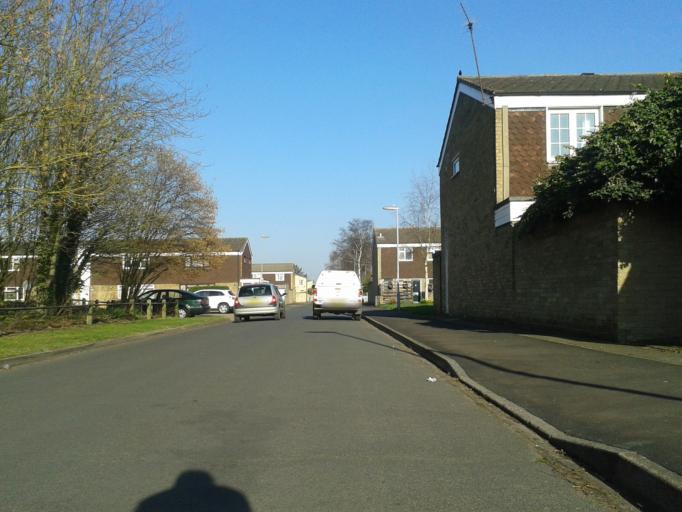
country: GB
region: England
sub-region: Cambridgeshire
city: Cambridge
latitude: 52.2291
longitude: 0.1320
